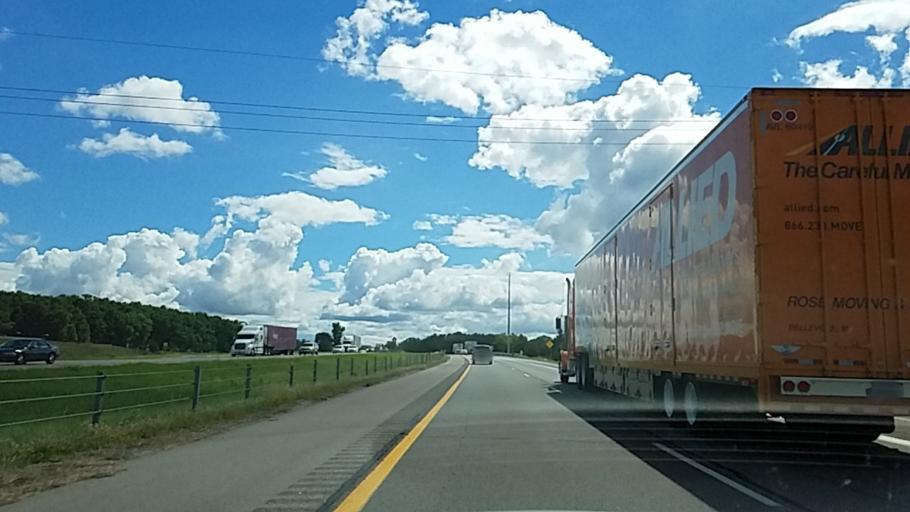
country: US
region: Michigan
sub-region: Livingston County
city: Whitmore Lake
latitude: 42.4697
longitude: -83.7562
